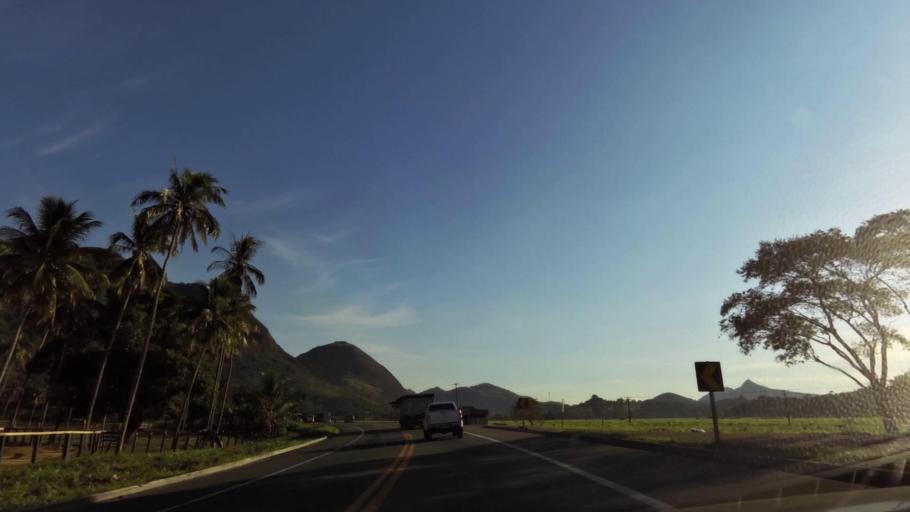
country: BR
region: Espirito Santo
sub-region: Guarapari
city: Guarapari
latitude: -20.6028
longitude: -40.5025
